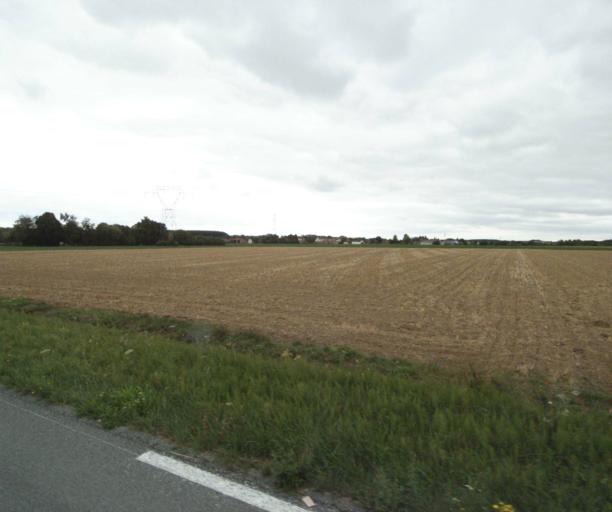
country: FR
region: Nord-Pas-de-Calais
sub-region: Departement du Nord
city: Fretin
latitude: 50.5663
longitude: 3.1579
